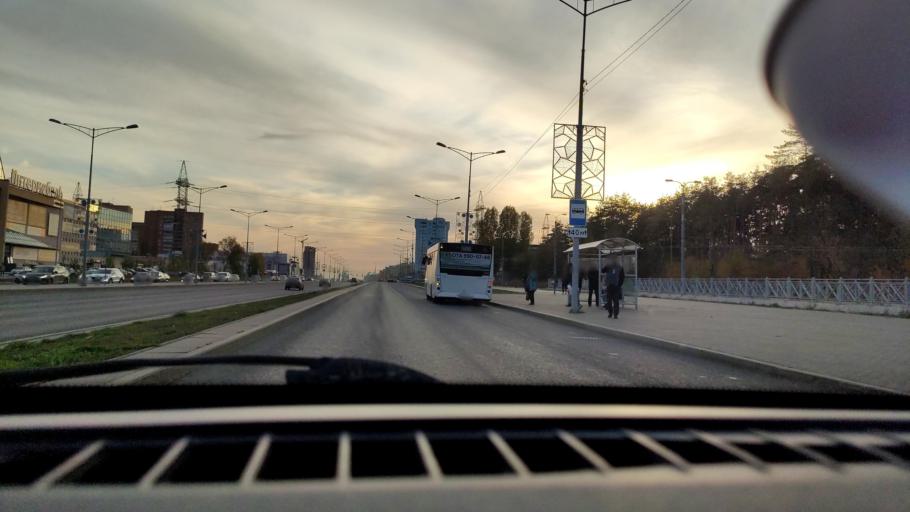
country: RU
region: Samara
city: Samara
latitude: 53.2638
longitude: 50.2437
